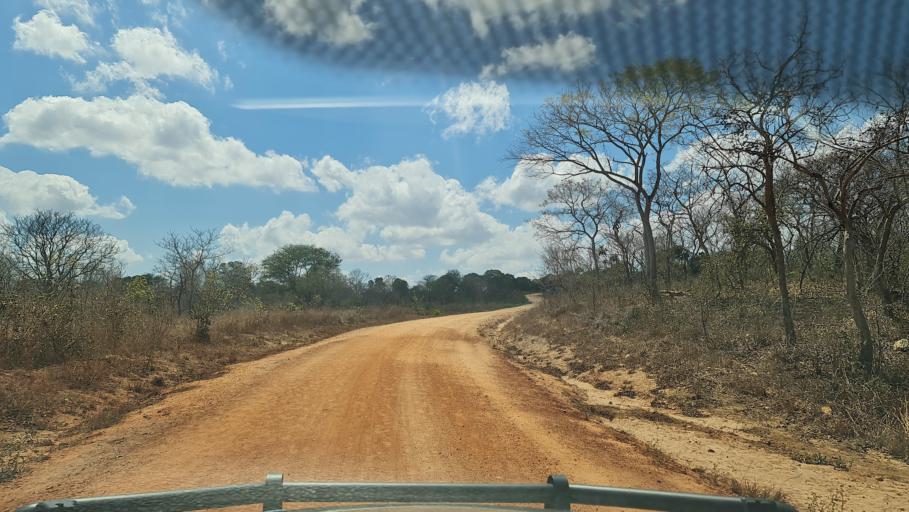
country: MZ
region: Nampula
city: Nacala
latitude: -14.1690
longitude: 40.2536
